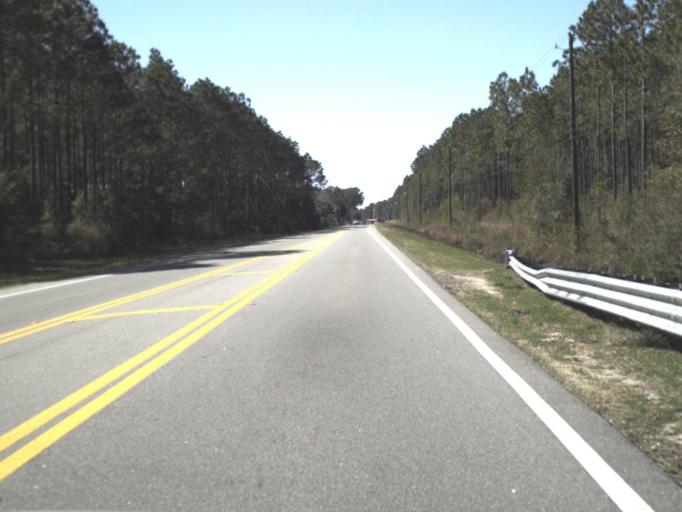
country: US
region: Florida
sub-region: Bay County
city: Laguna Beach
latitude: 30.2987
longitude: -85.8435
